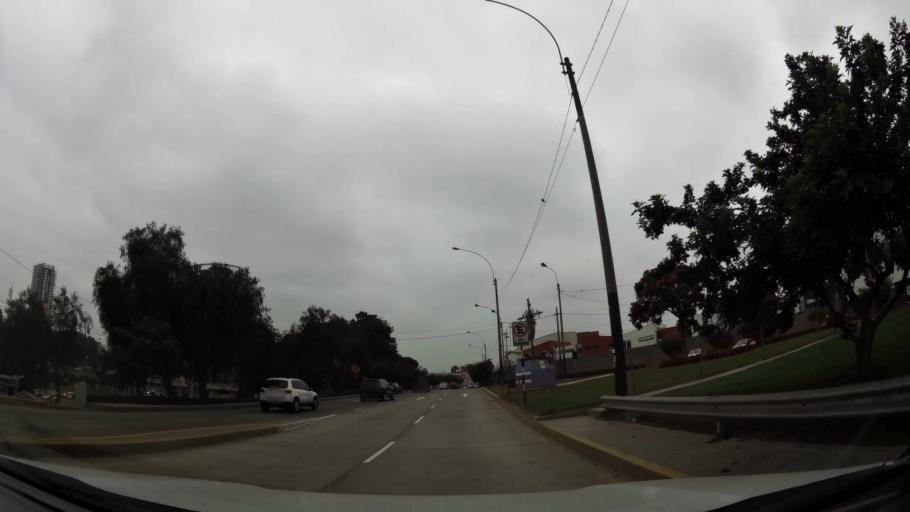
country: PE
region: Lima
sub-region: Lima
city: San Luis
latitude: -12.0926
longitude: -77.0226
